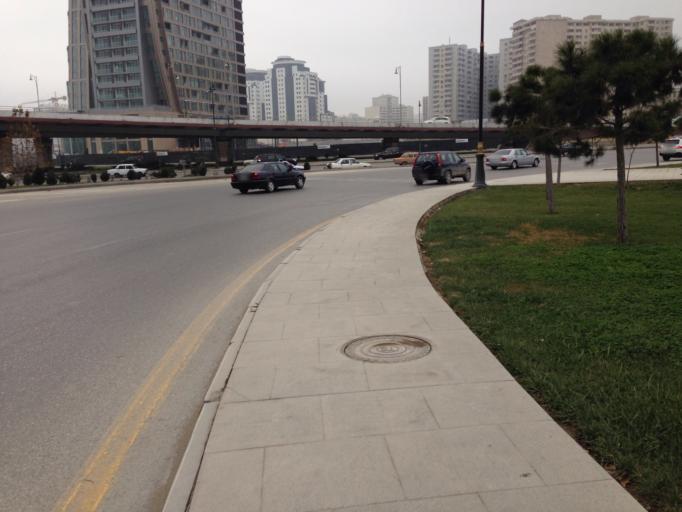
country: AZ
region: Baki
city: Baku
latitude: 40.3892
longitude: 49.8676
